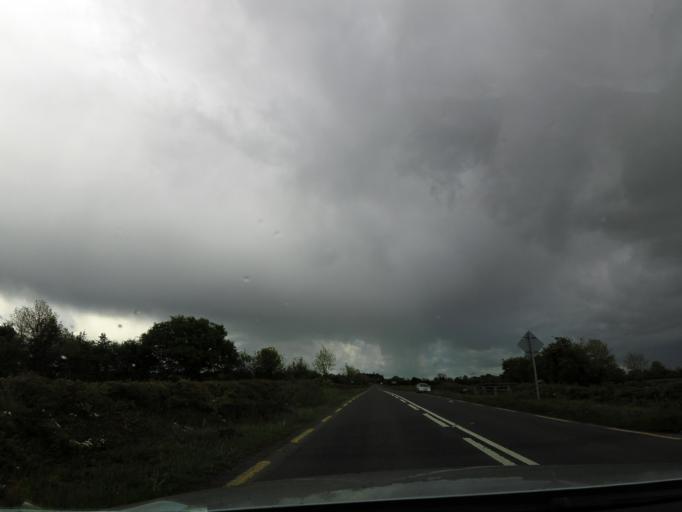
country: IE
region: Munster
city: Thurles
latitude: 52.7176
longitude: -7.8269
